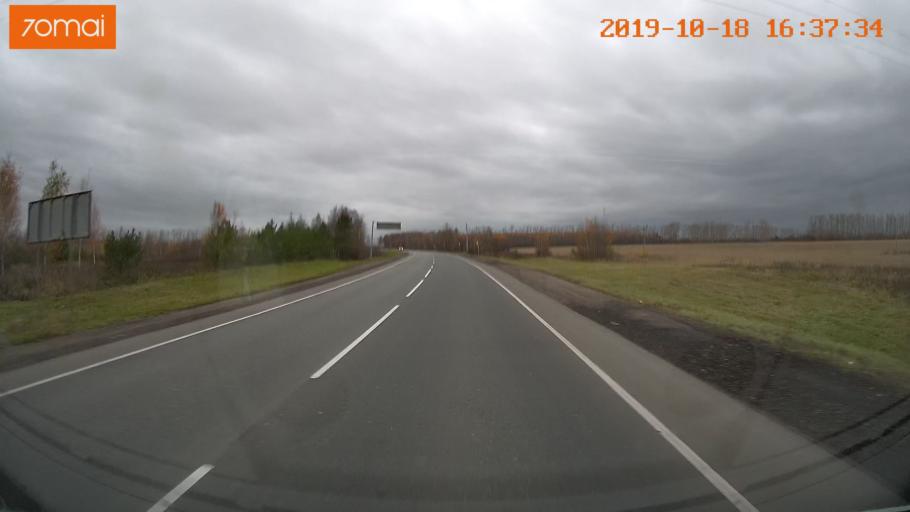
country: RU
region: Vladimir
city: Suzdal'
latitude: 56.4236
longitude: 40.4767
